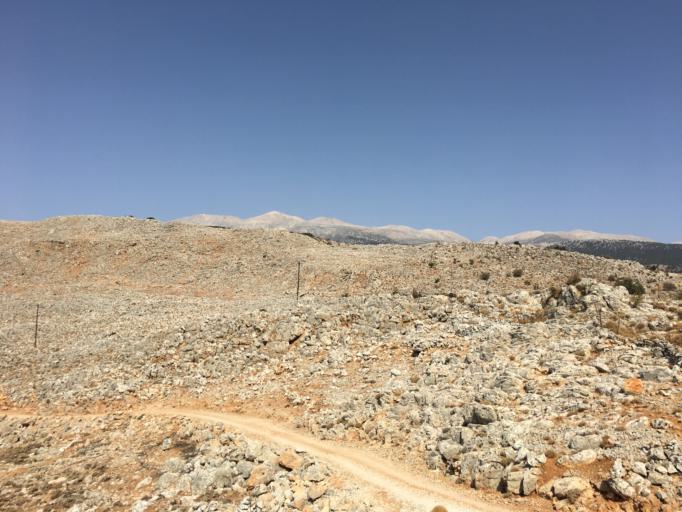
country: GR
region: Crete
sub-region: Nomos Chanias
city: Chora Sfakion
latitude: 35.2087
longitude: 24.0955
